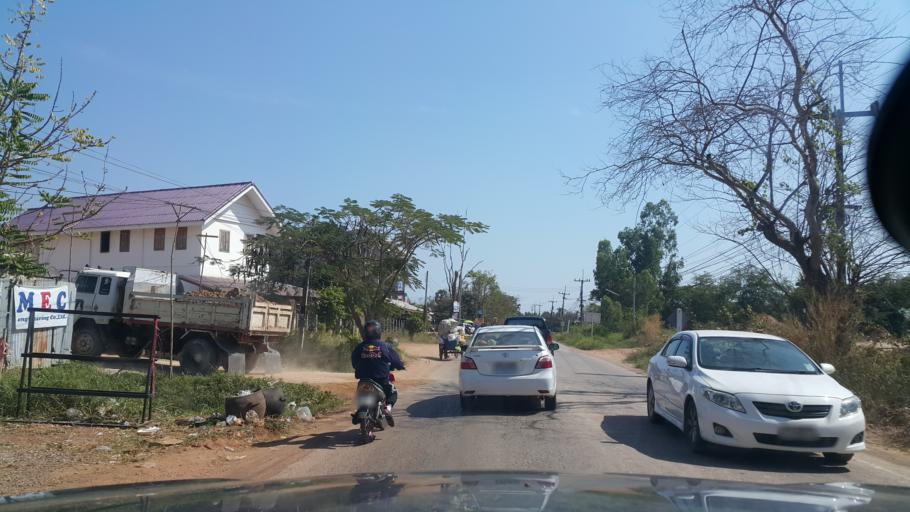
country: TH
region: Changwat Udon Thani
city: Udon Thani
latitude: 17.4699
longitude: 102.7740
